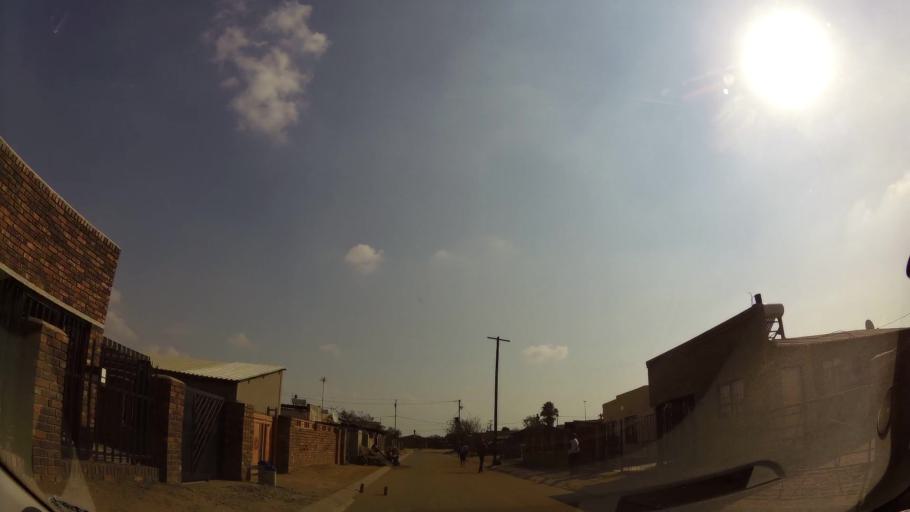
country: ZA
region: Gauteng
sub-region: Ekurhuleni Metropolitan Municipality
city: Springs
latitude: -26.1107
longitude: 28.4785
